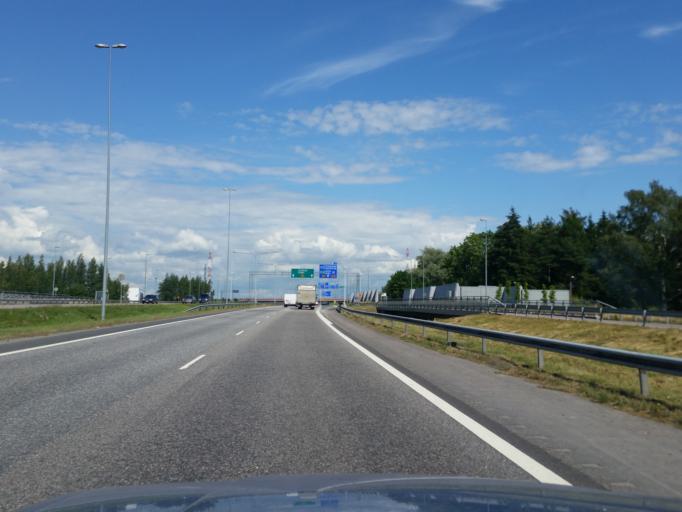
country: FI
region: Uusimaa
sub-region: Helsinki
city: Vantaa
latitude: 60.2812
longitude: 24.9784
